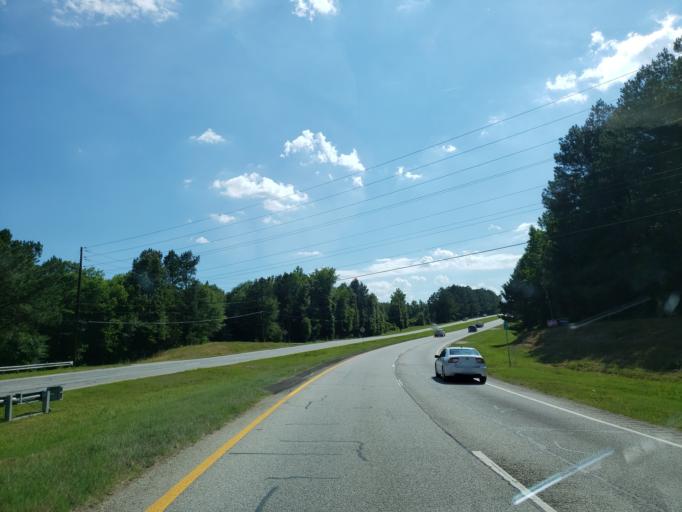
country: US
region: Georgia
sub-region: Paulding County
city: Dallas
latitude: 33.9158
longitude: -84.8789
